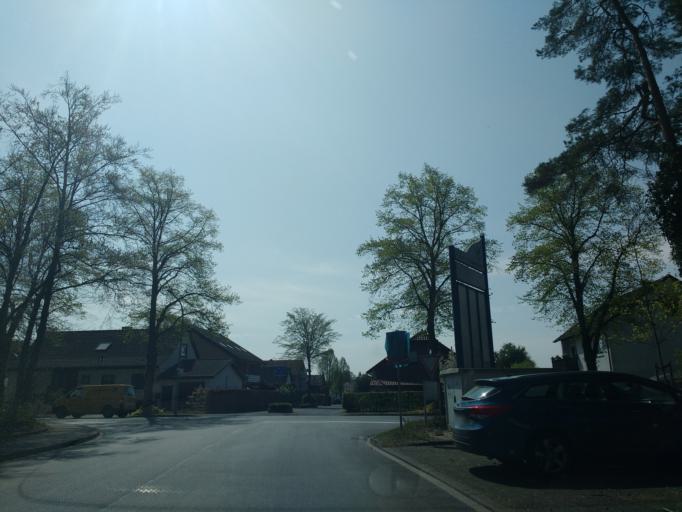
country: DE
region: North Rhine-Westphalia
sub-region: Regierungsbezirk Detmold
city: Hovelhof
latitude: 51.8280
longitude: 8.6534
